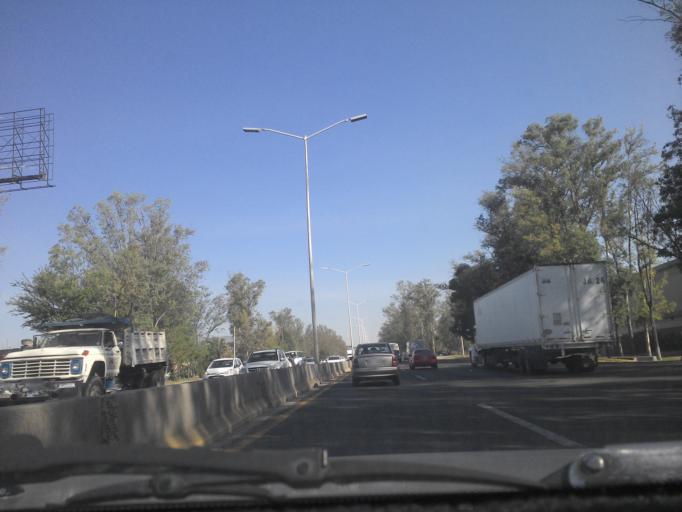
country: MX
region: Jalisco
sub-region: Tlajomulco de Zuniga
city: La Tijera
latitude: 20.6194
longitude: -103.4304
